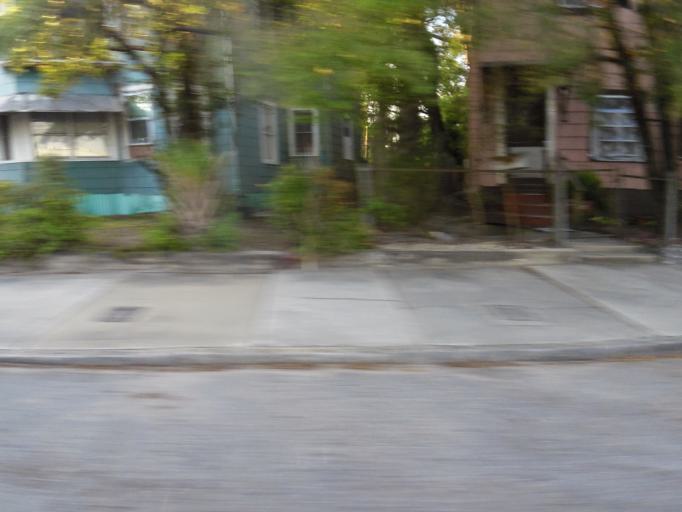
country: US
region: Florida
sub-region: Duval County
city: Jacksonville
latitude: 30.3230
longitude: -81.6955
